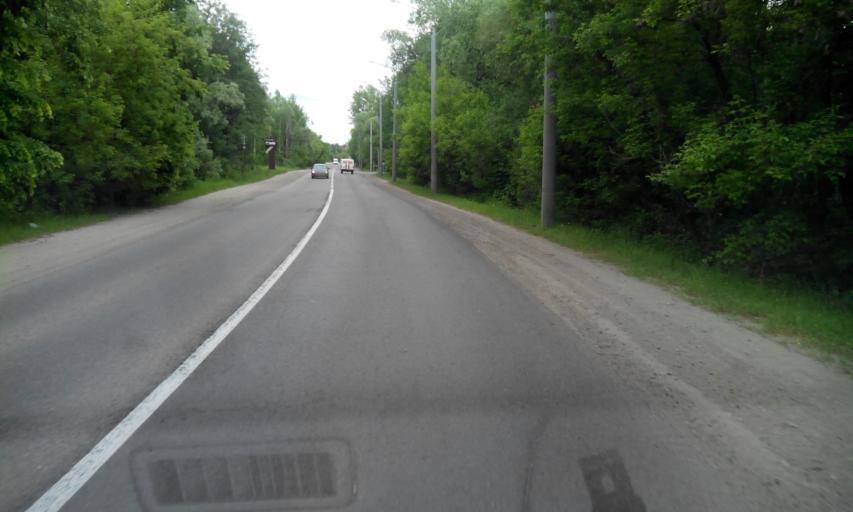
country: RU
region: Penza
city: Penza
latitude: 53.2118
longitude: 45.0842
